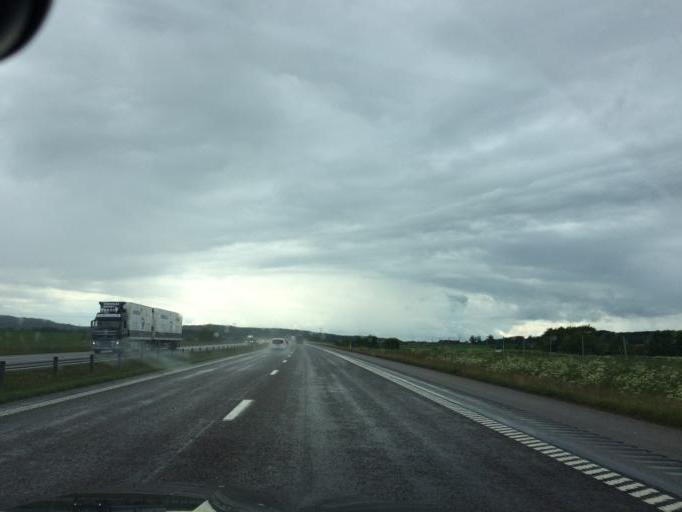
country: SE
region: Halland
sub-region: Halmstads Kommun
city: Getinge
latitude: 56.7986
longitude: 12.7740
